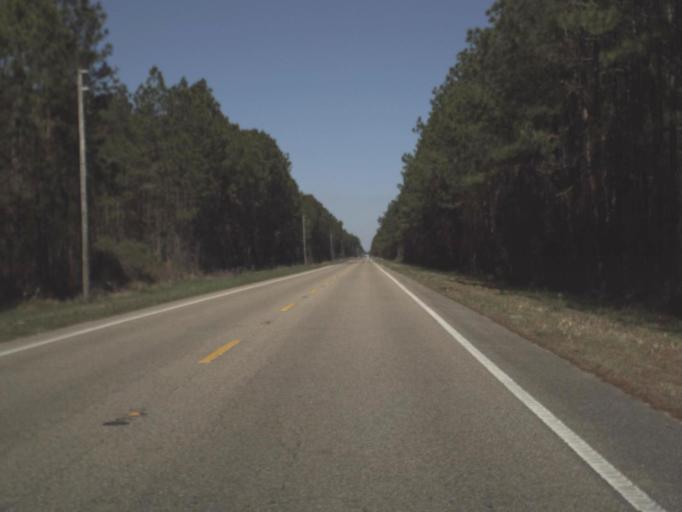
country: US
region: Florida
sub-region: Gulf County
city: Port Saint Joe
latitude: 29.8418
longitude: -85.2678
